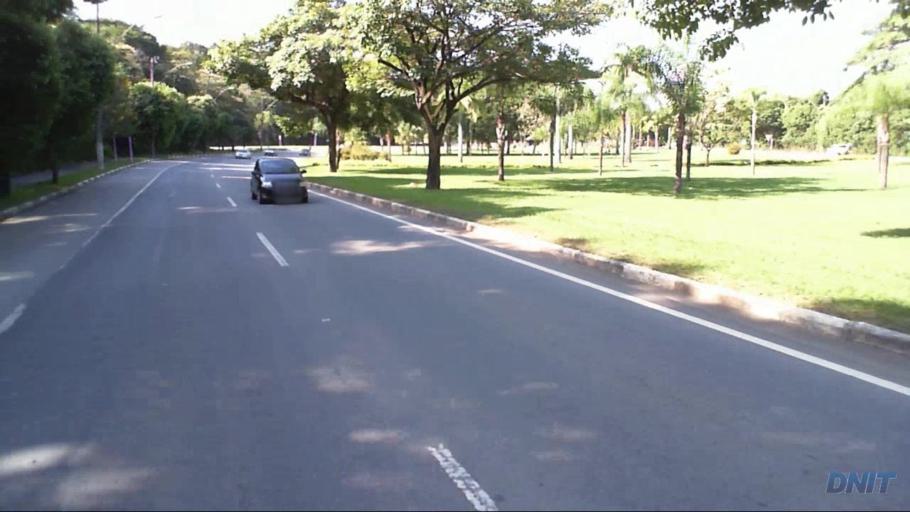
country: BR
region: Minas Gerais
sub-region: Ipatinga
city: Ipatinga
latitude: -19.4876
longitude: -42.5593
